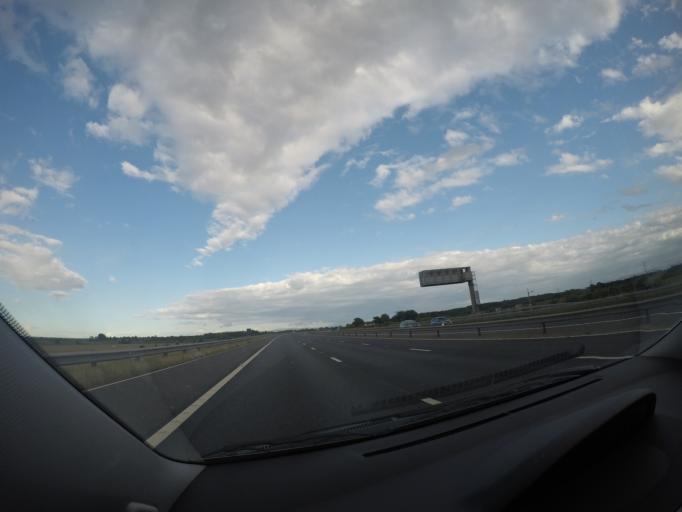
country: GB
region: Scotland
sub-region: Dumfries and Galloway
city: Gretna
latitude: 54.9778
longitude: -3.0157
